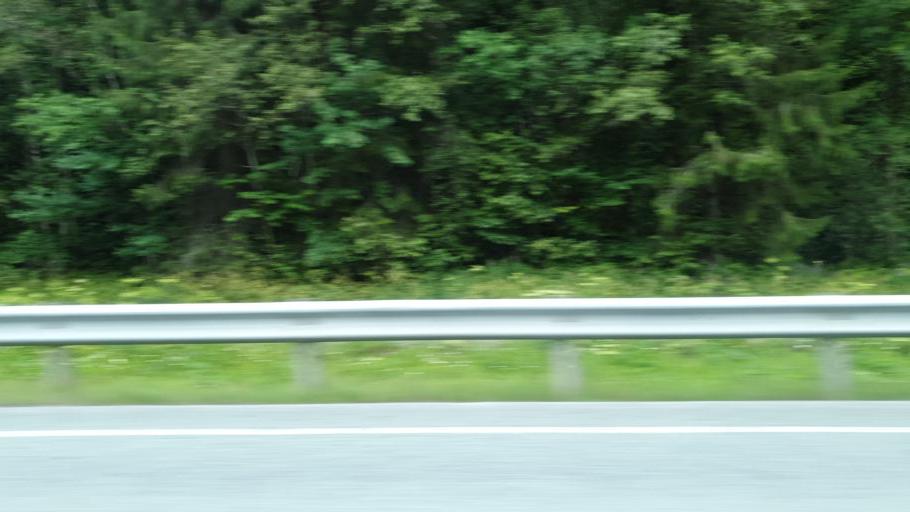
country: NO
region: Sor-Trondelag
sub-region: Midtre Gauldal
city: Storen
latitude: 63.0213
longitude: 10.2484
